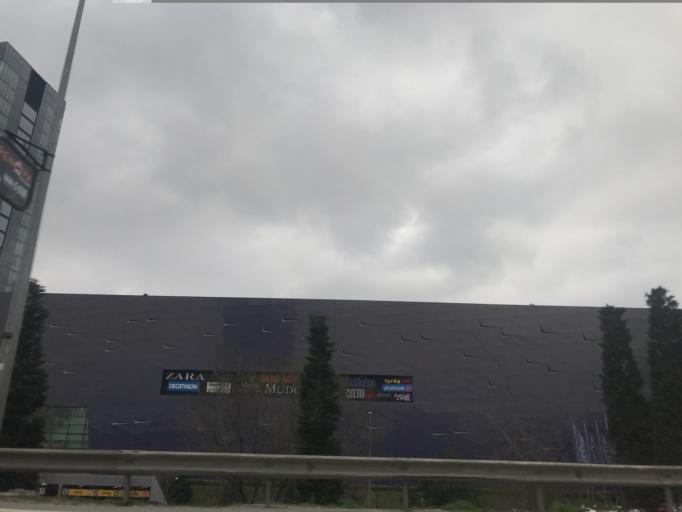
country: TR
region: Istanbul
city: Umraniye
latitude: 41.0274
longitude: 29.1274
